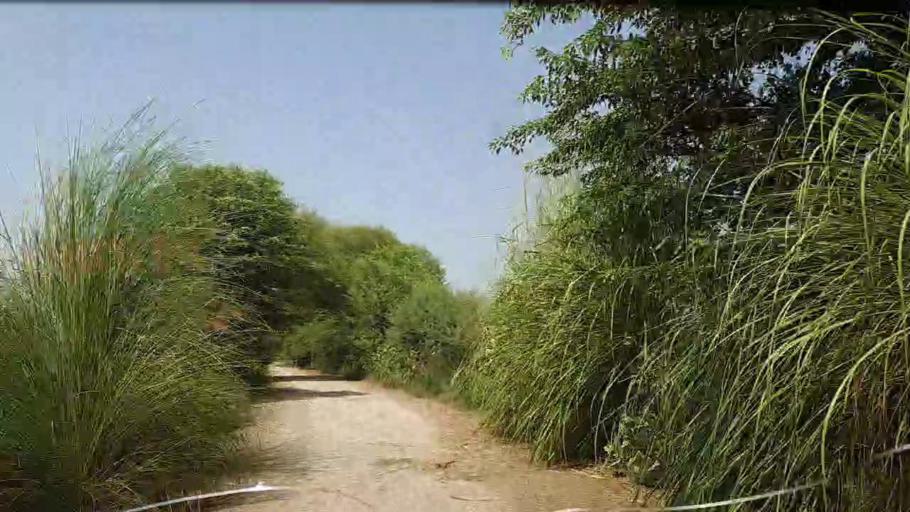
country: PK
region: Sindh
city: Ghotki
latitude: 28.0698
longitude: 69.3175
